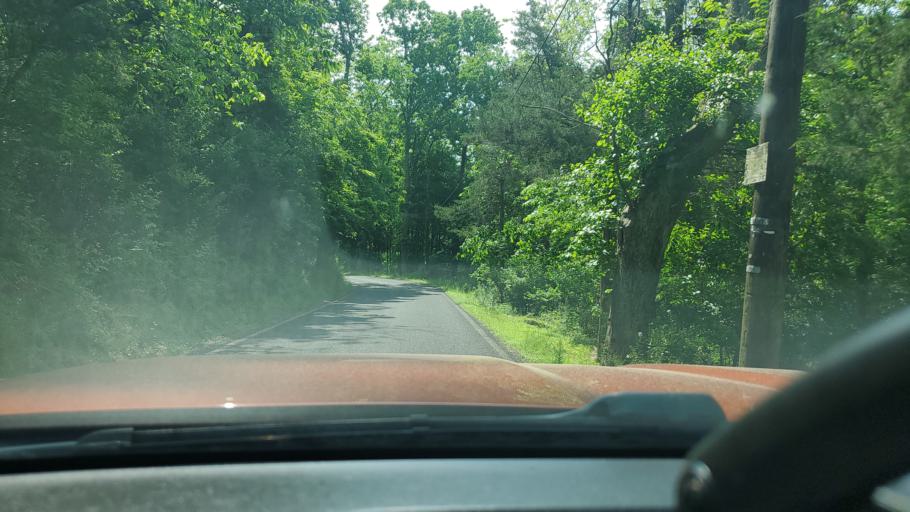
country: US
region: Pennsylvania
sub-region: Montgomery County
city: Limerick
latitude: 40.2741
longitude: -75.5097
